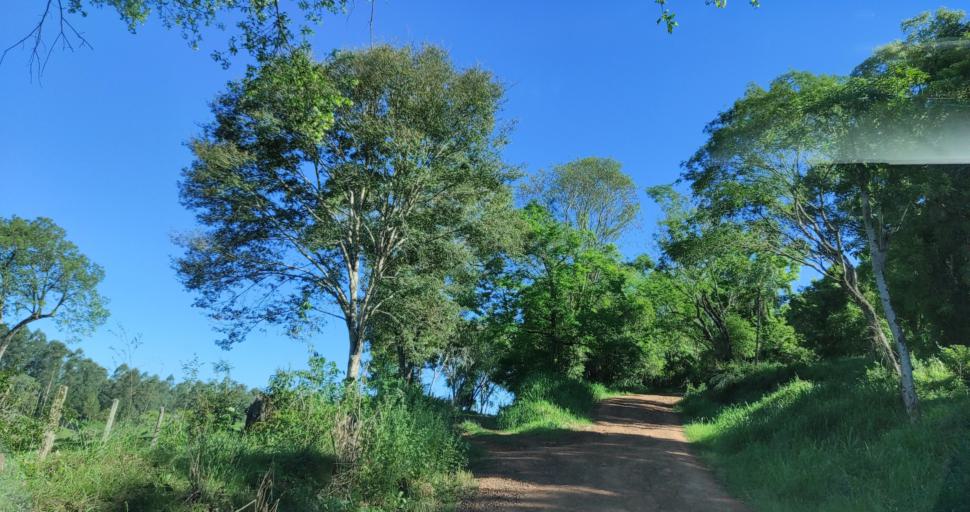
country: AR
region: Misiones
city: Capiovi
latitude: -26.9232
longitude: -55.0796
